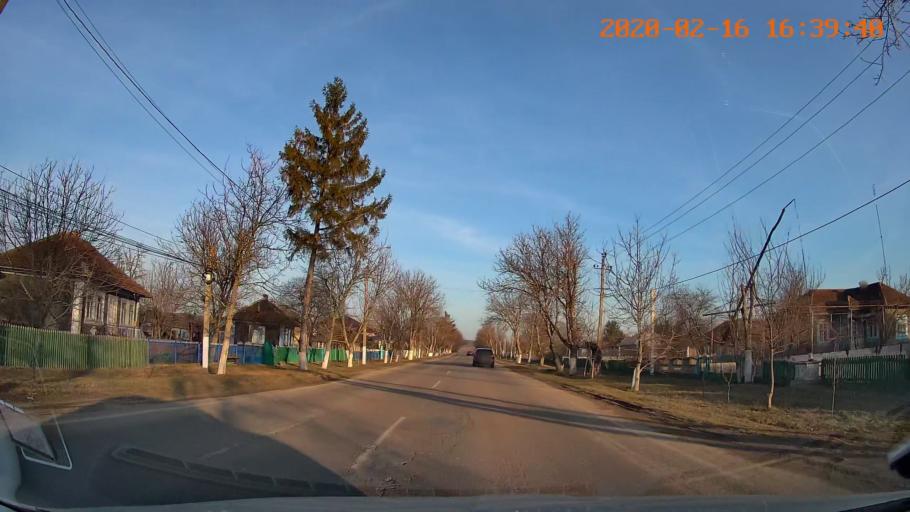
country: RO
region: Botosani
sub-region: Comuna Radauti-Prut
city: Rediu
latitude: 48.2697
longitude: 26.7471
